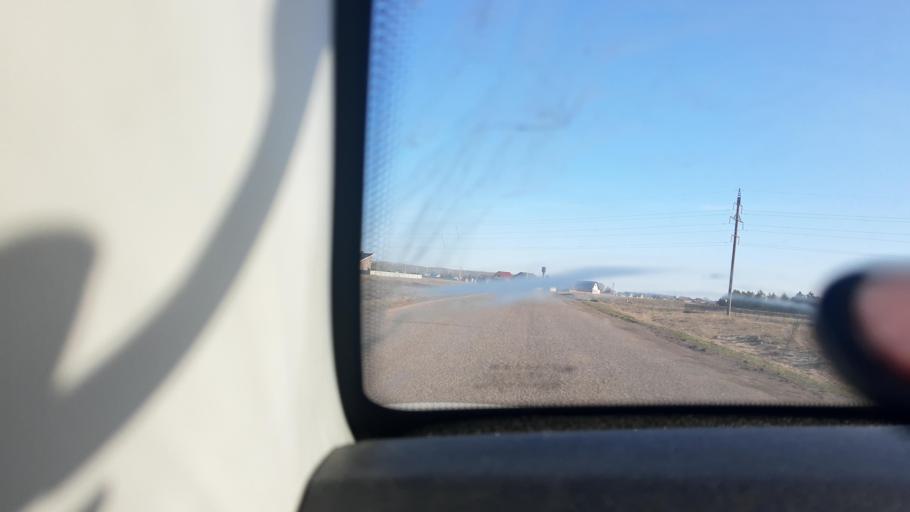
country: RU
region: Bashkortostan
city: Asanovo
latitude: 54.9576
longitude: 55.5349
